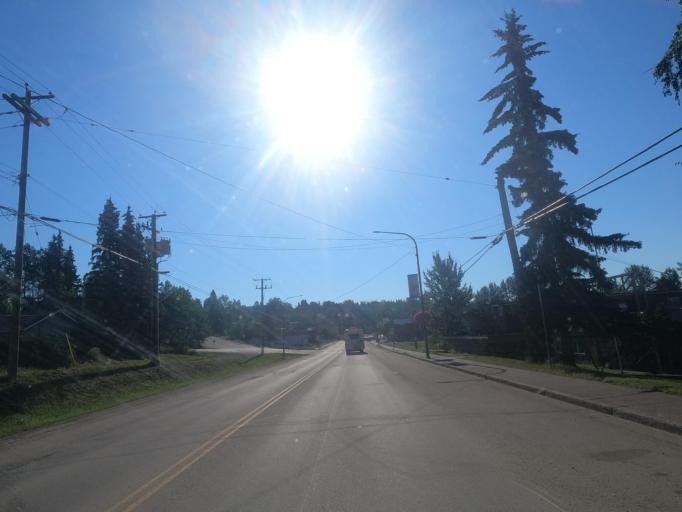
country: CA
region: British Columbia
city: Burns Lake
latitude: 54.2343
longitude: -125.7670
